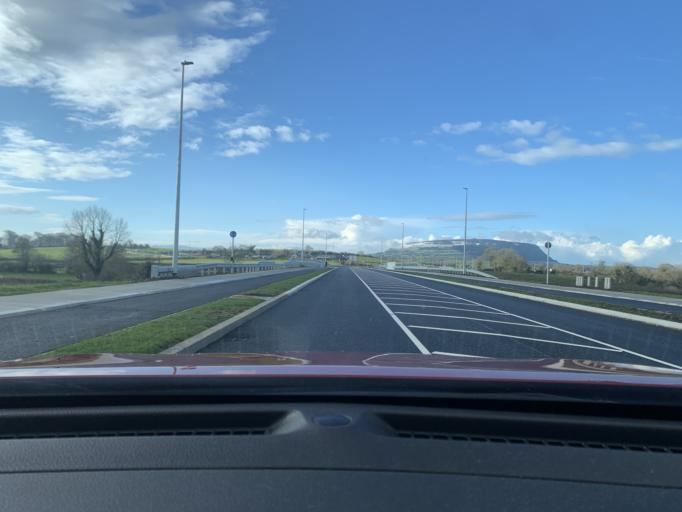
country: IE
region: Connaught
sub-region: Sligo
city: Sligo
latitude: 54.2604
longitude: -8.4899
